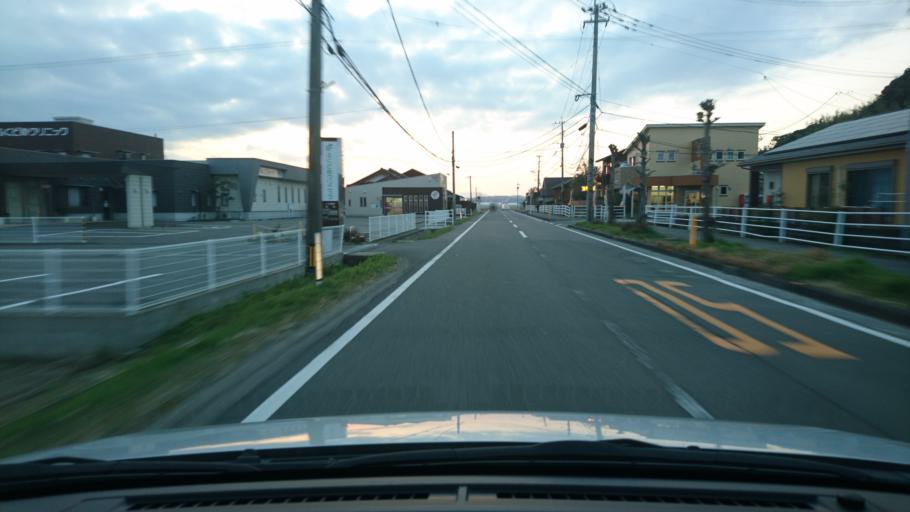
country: JP
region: Miyazaki
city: Miyazaki-shi
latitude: 31.8473
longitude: 131.4265
